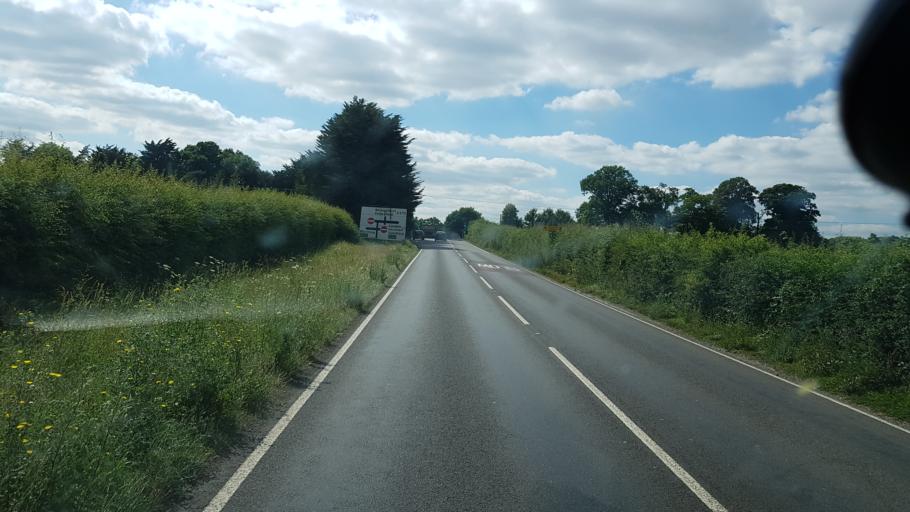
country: GB
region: England
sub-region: West Sussex
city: Southwater
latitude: 50.9915
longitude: -0.3374
